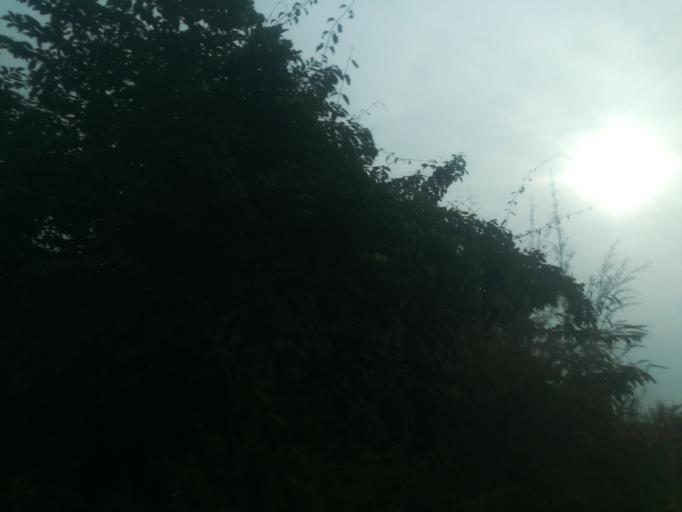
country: NG
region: Ogun
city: Ayetoro
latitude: 7.2390
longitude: 3.1278
